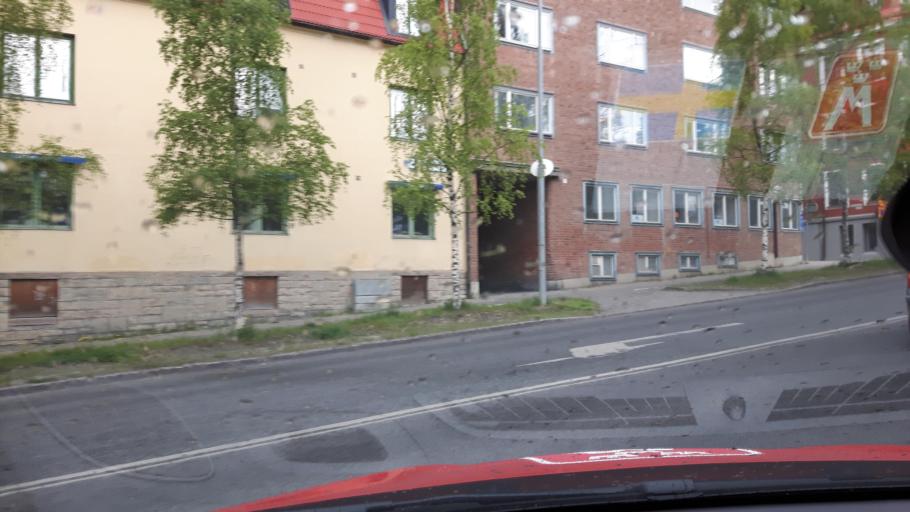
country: SE
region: Jaemtland
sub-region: OEstersunds Kommun
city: Ostersund
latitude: 63.1718
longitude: 14.6371
